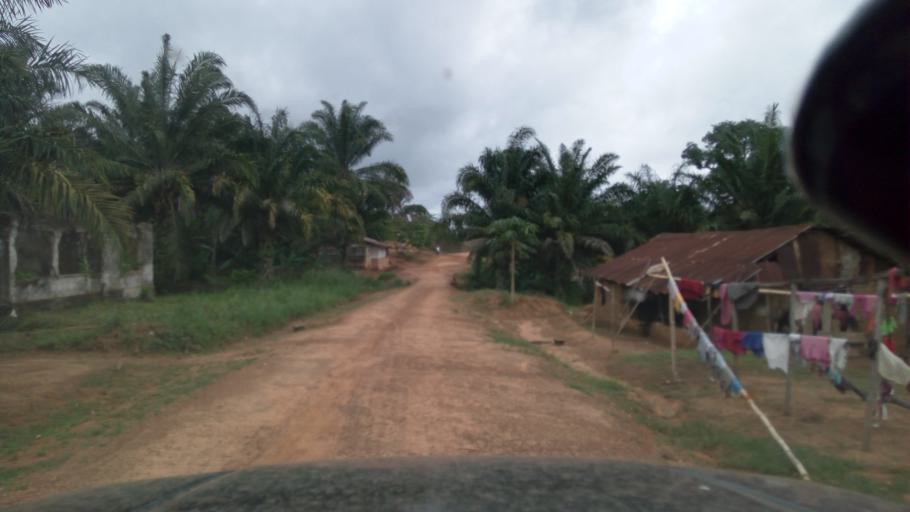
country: SL
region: Eastern Province
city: Panguma
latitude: 8.1535
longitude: -11.1729
